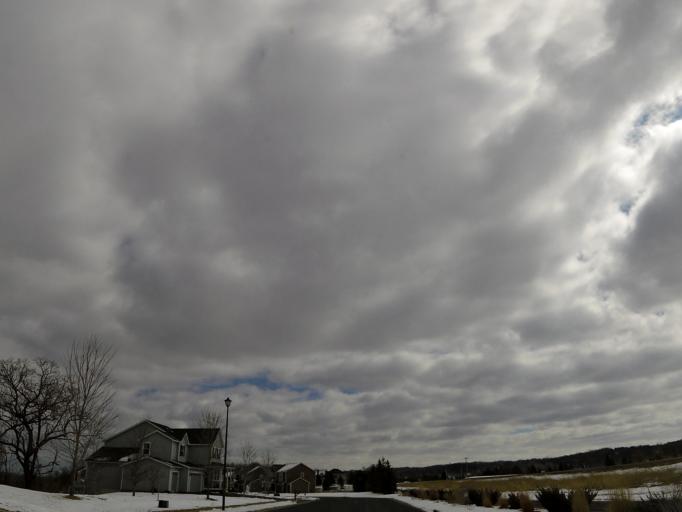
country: US
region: Minnesota
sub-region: Scott County
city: Prior Lake
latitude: 44.7674
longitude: -93.4333
